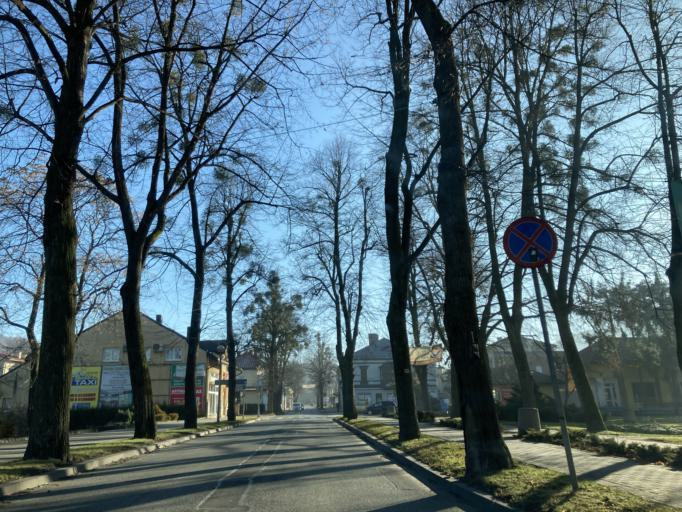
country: PL
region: Silesian Voivodeship
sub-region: Powiat cieszynski
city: Ustron
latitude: 49.7190
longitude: 18.8129
